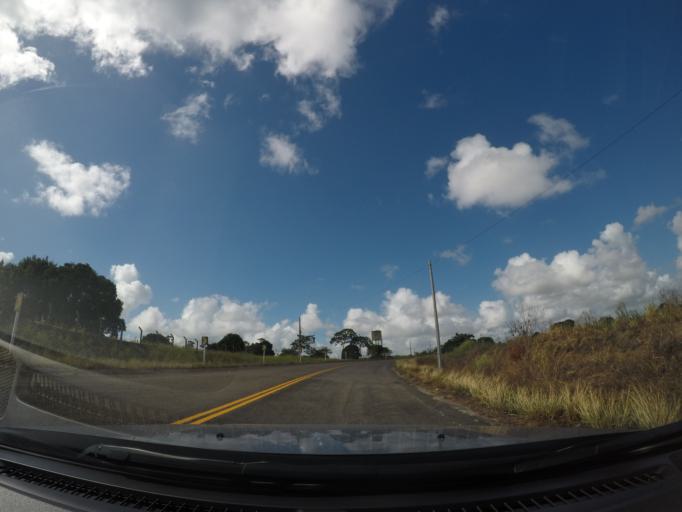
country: BR
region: Paraiba
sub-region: Pitimbu
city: Pitimbu
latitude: -7.3774
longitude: -34.8230
